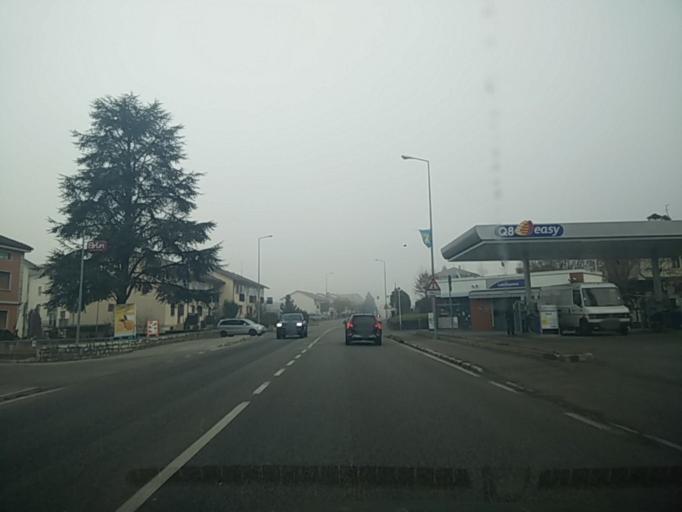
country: IT
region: Veneto
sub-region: Provincia di Belluno
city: Feltre
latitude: 46.0243
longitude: 11.9245
